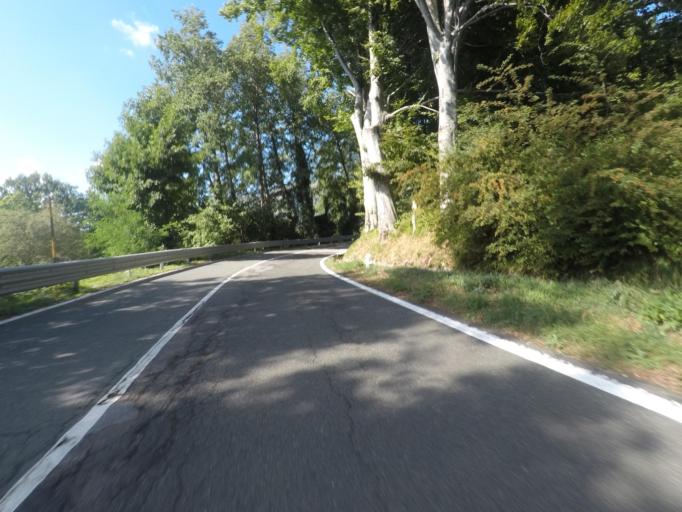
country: IT
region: Tuscany
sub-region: Provincia di Massa-Carrara
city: Comano
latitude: 44.2787
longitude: 10.1855
